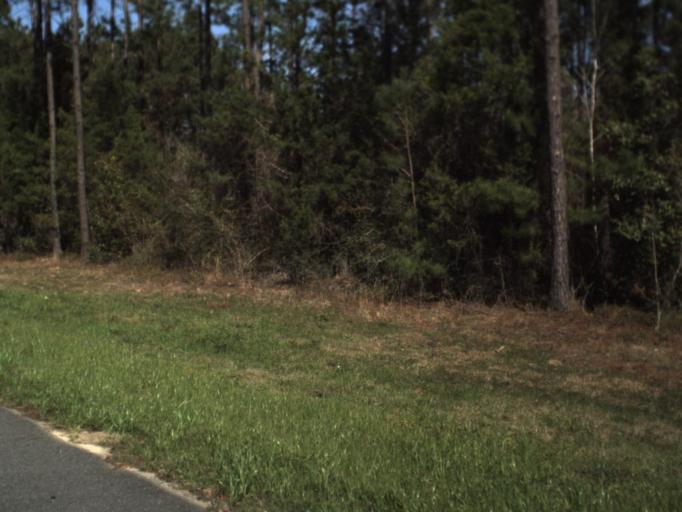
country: US
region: Florida
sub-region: Calhoun County
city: Blountstown
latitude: 30.3149
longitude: -85.1279
